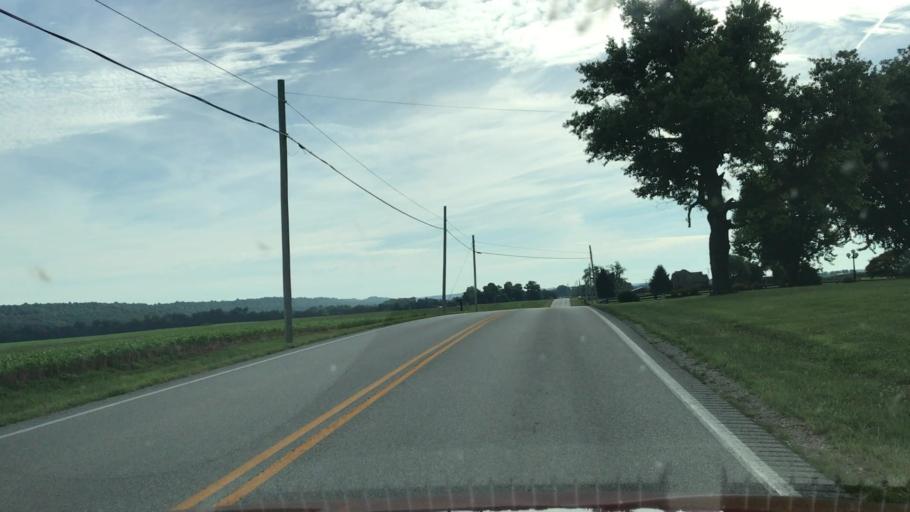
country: US
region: Kentucky
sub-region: Edmonson County
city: Brownsville
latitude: 37.0619
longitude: -86.2897
